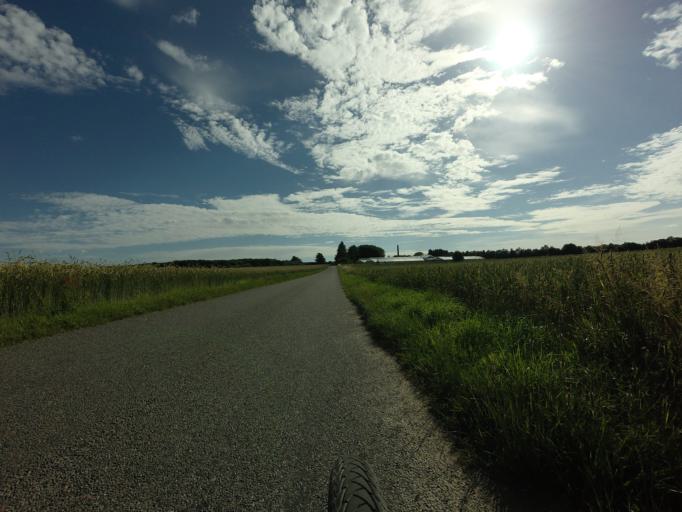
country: DK
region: Central Jutland
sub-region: Skanderborg Kommune
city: Horning
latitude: 56.0941
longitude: 10.0157
